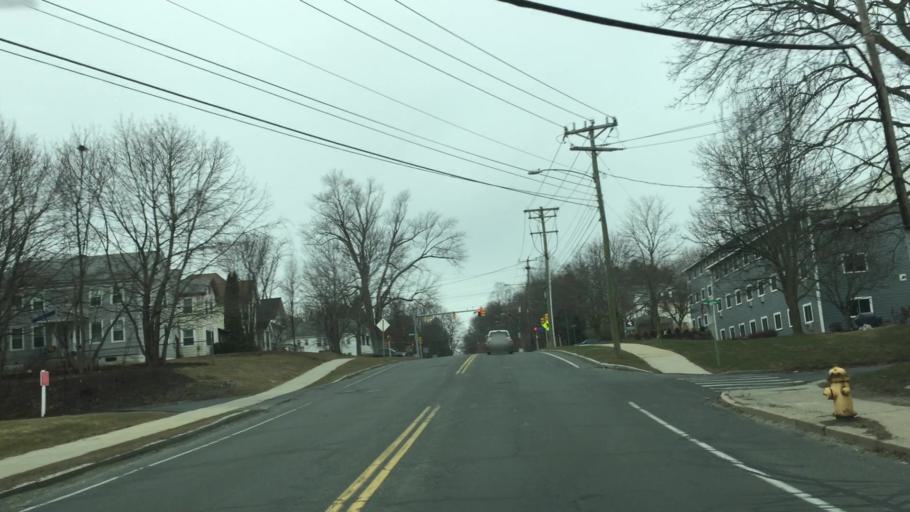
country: US
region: Massachusetts
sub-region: Berkshire County
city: Pittsfield
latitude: 42.4500
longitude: -73.2636
